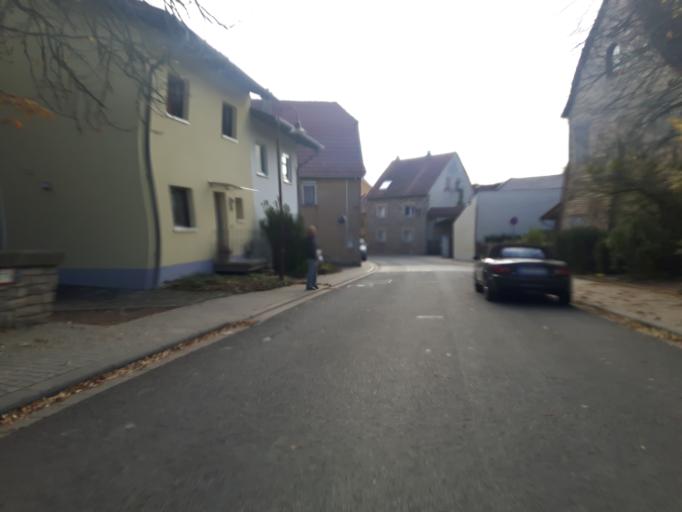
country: DE
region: Rheinland-Pfalz
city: Eppelsheim
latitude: 49.7055
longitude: 8.1647
